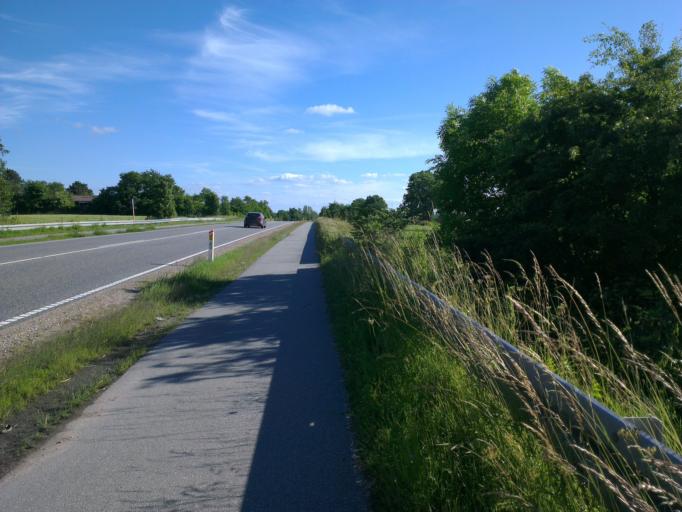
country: DK
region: Capital Region
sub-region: Frederikssund Kommune
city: Skibby
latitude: 55.7684
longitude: 11.9591
